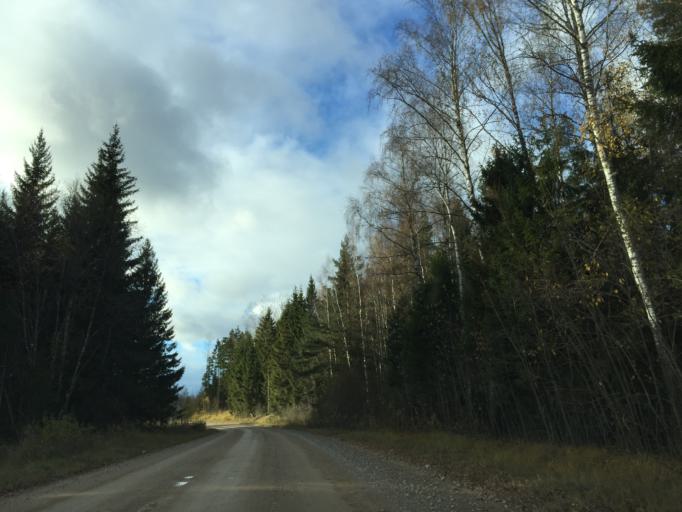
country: LV
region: Tukuma Rajons
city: Tukums
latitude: 56.9810
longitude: 23.0087
